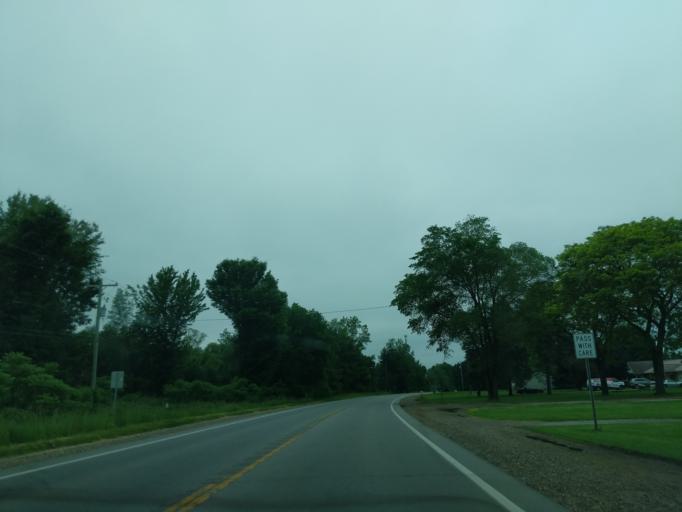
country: US
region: Michigan
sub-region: Branch County
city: Quincy
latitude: 41.9487
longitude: -84.8113
